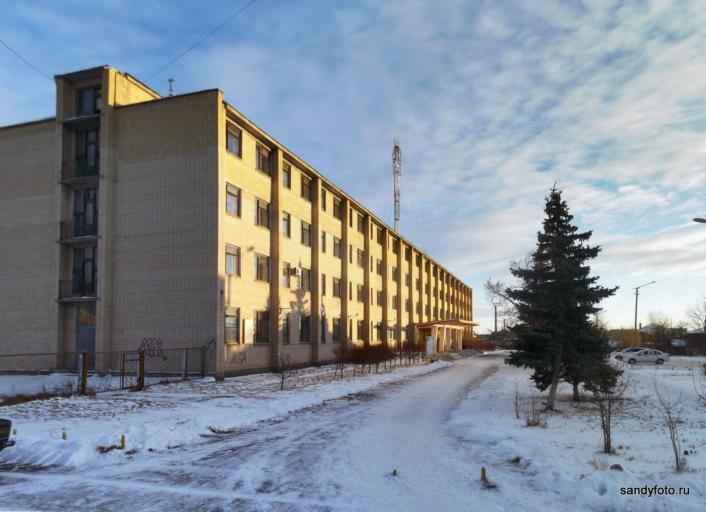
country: RU
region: Chelyabinsk
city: Troitsk
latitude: 54.0814
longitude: 61.5619
